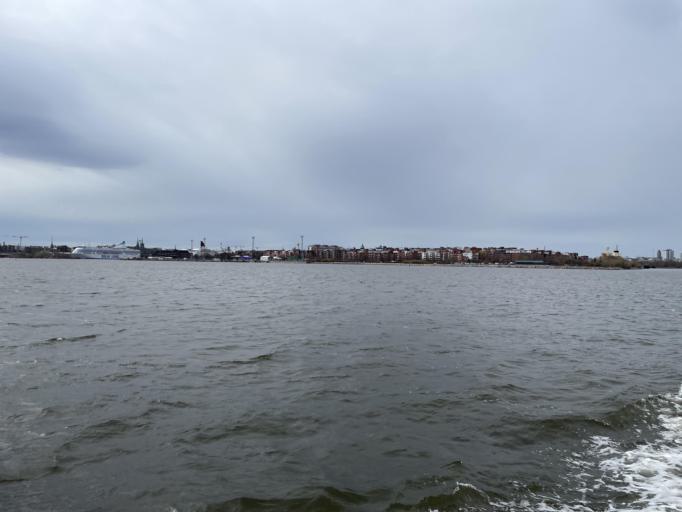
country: FI
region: Uusimaa
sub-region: Helsinki
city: Helsinki
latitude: 60.1643
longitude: 24.9874
